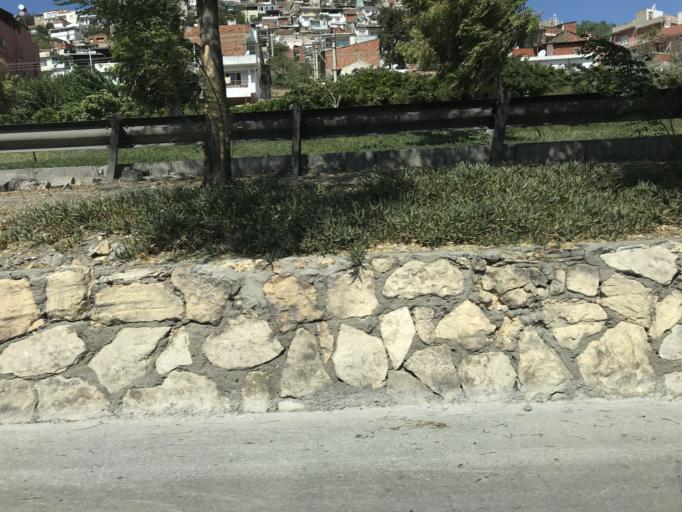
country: TR
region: Izmir
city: Buca
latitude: 38.4119
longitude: 27.1561
